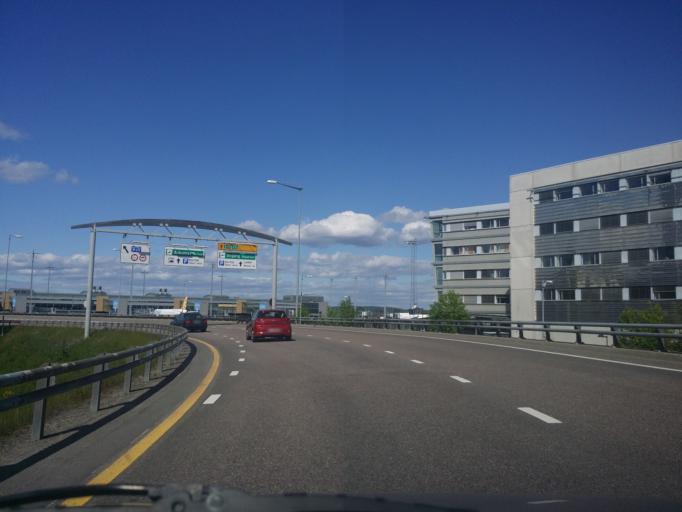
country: NO
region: Akershus
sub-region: Nannestad
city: Teigebyen
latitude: 60.1900
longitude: 11.0984
